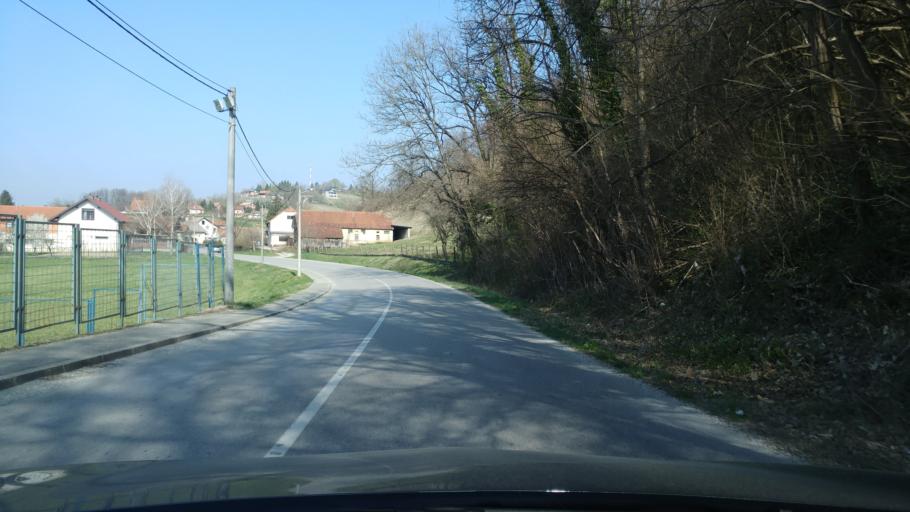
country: HR
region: Zagrebacka
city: Pojatno
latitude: 45.9174
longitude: 15.7750
